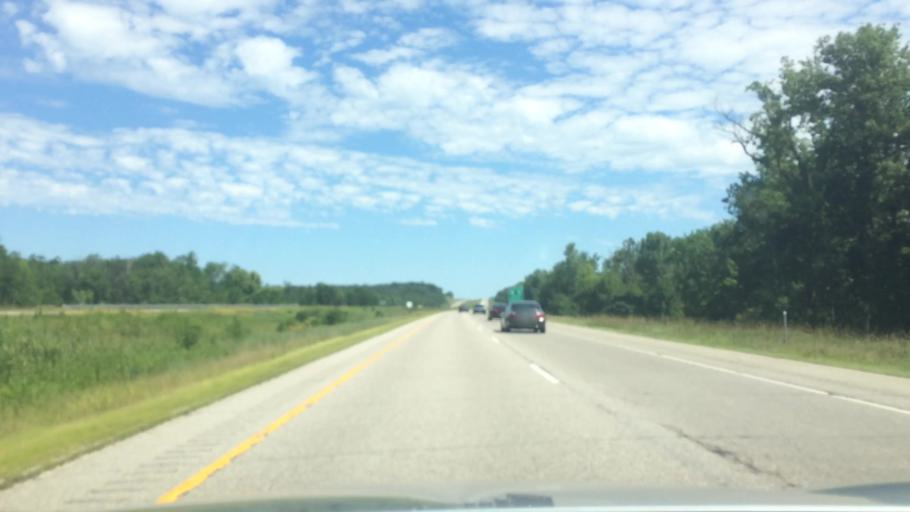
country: US
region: Wisconsin
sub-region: Marquette County
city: Westfield
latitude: 43.7681
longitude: -89.4846
